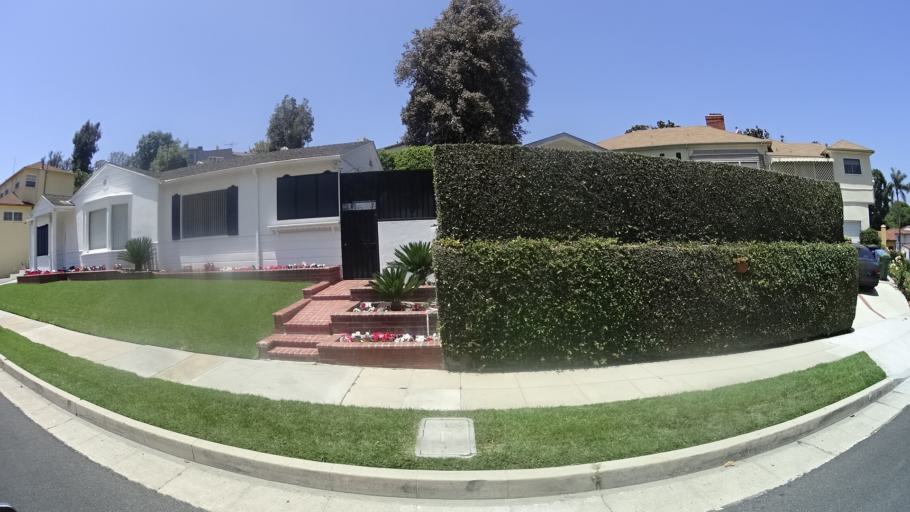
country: US
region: California
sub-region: Los Angeles County
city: View Park-Windsor Hills
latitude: 33.9958
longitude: -118.3412
